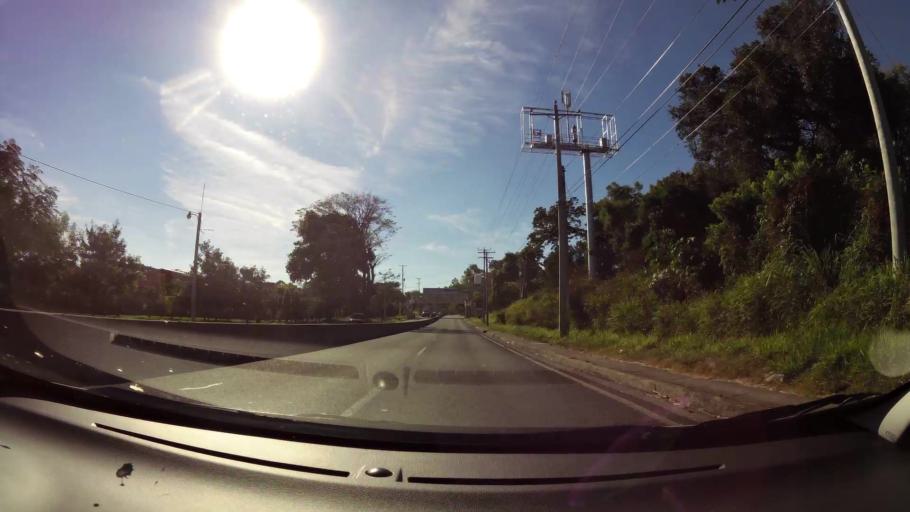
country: SV
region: Santa Ana
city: Santa Ana
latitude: 13.9607
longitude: -89.5785
